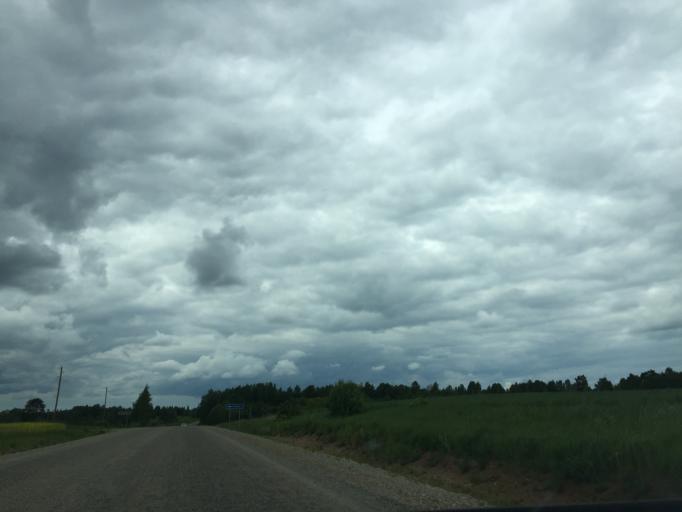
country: LV
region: Dagda
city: Dagda
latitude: 56.0498
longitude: 27.5733
